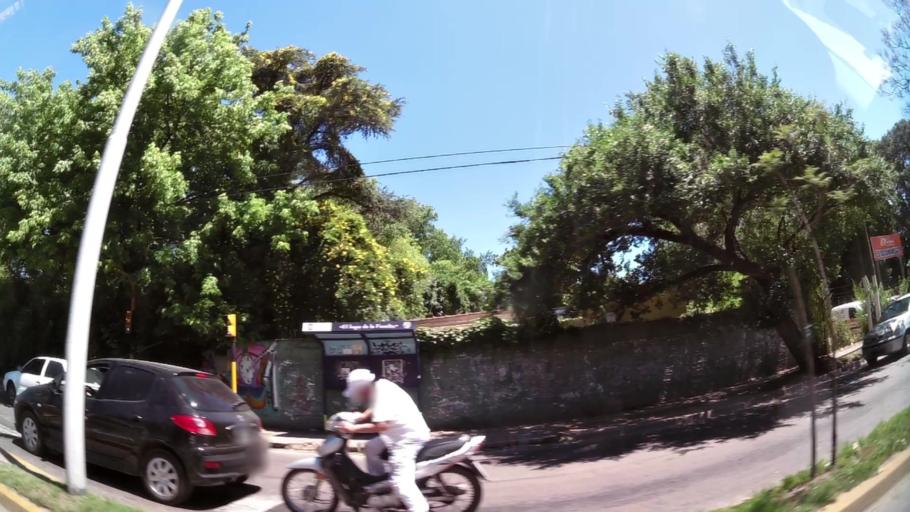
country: AR
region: Buenos Aires
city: Hurlingham
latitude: -34.5058
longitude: -58.6861
